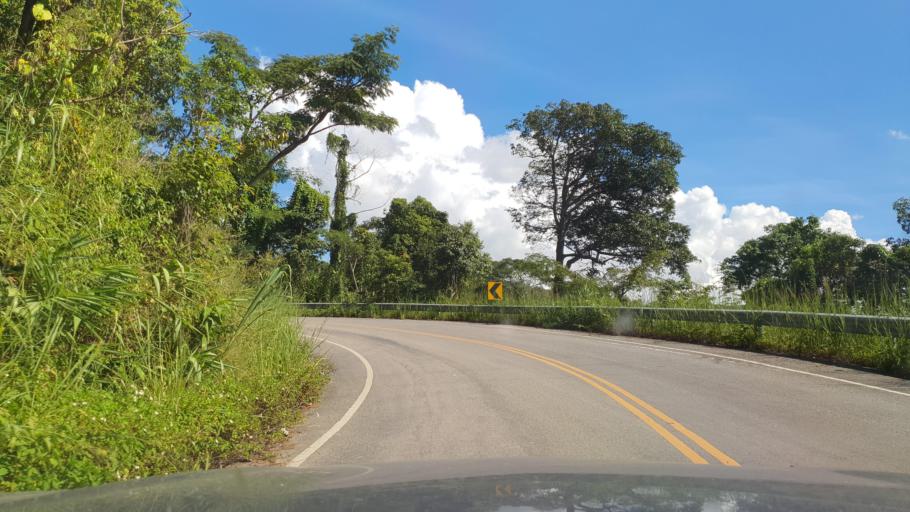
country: TH
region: Chiang Mai
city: Phrao
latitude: 19.3059
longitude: 99.3447
